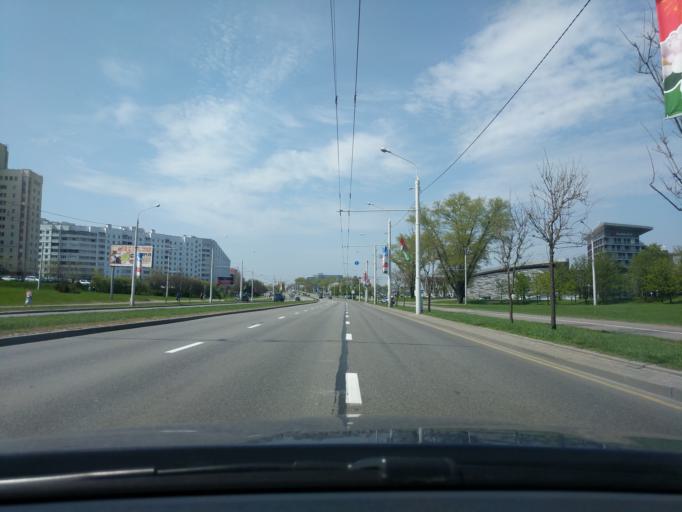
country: BY
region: Minsk
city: Minsk
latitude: 53.9299
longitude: 27.5134
